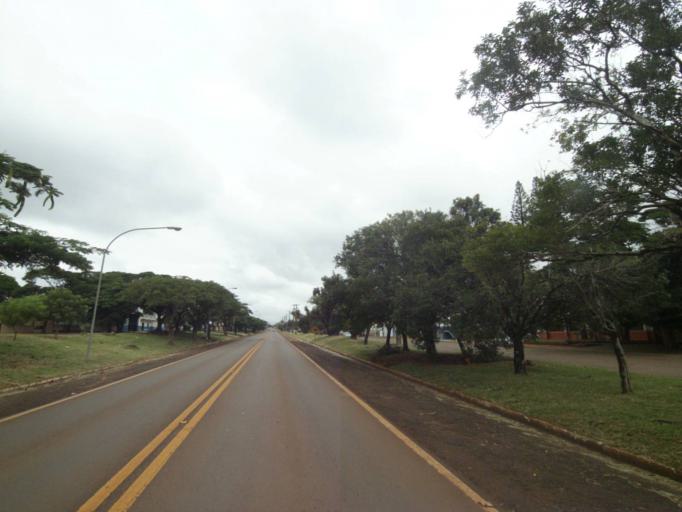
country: BR
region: Parana
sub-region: Campo Mourao
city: Campo Mourao
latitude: -24.0225
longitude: -52.3642
